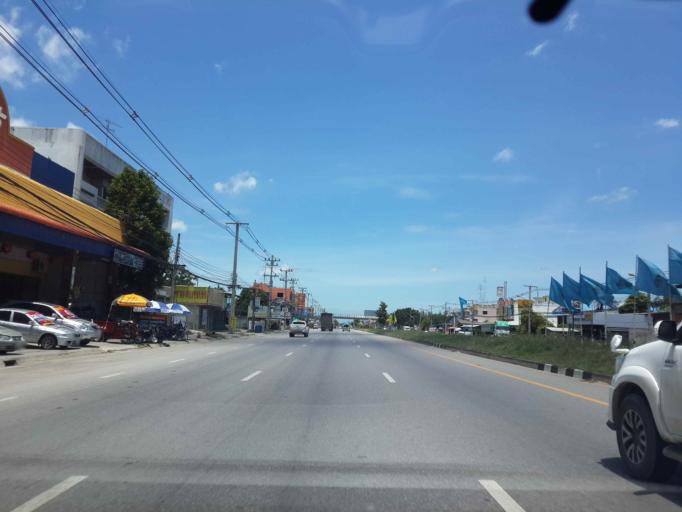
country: TH
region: Phetchaburi
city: Cha-am
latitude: 12.8357
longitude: 99.9326
